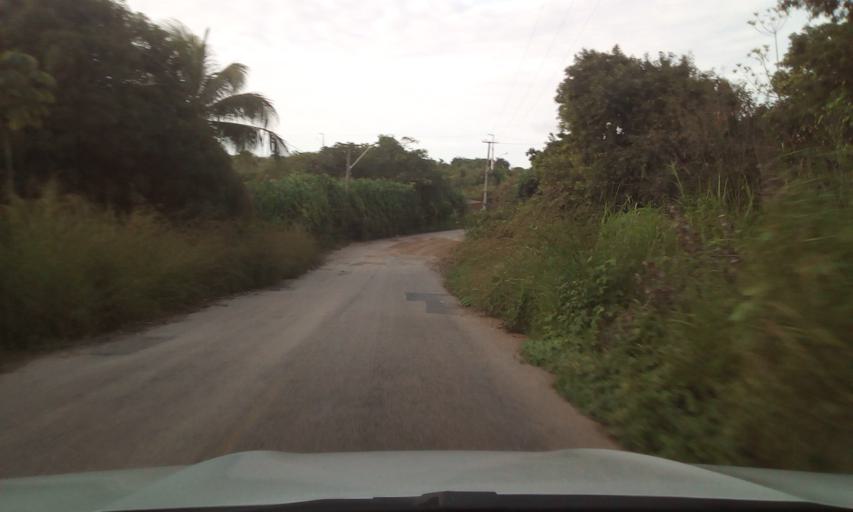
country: BR
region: Paraiba
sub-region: Conde
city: Conde
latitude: -7.2176
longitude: -34.8100
